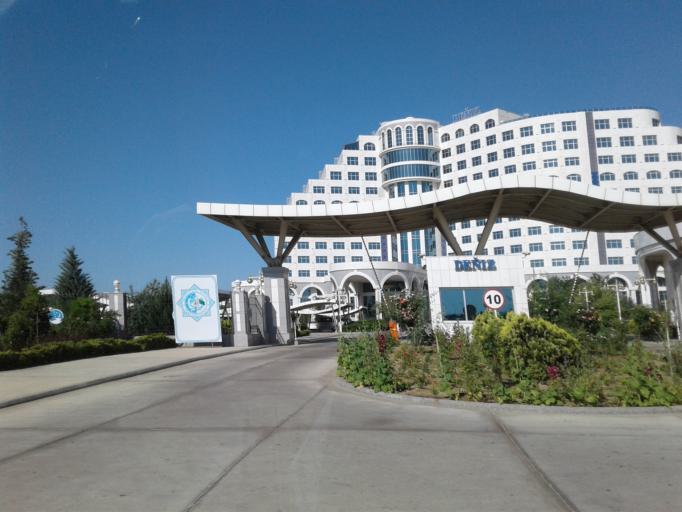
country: TM
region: Balkan
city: Turkmenbasy
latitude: 39.9639
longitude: 52.8335
